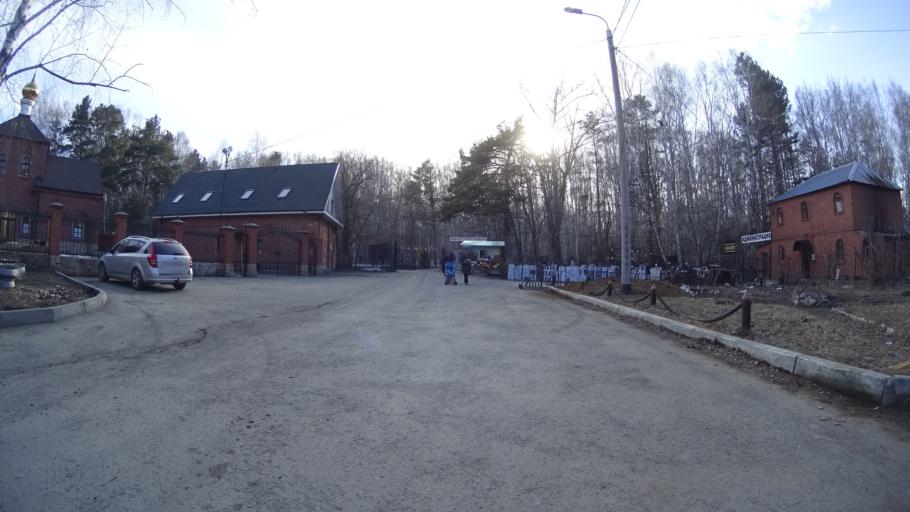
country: RU
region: Chelyabinsk
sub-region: Gorod Chelyabinsk
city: Chelyabinsk
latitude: 55.1287
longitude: 61.3559
